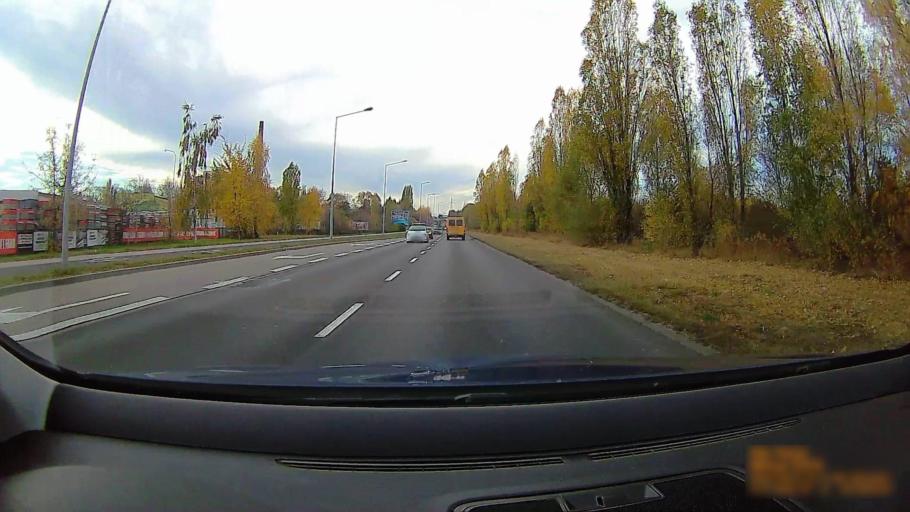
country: PL
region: Greater Poland Voivodeship
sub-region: Kalisz
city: Kalisz
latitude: 51.7689
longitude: 18.0690
